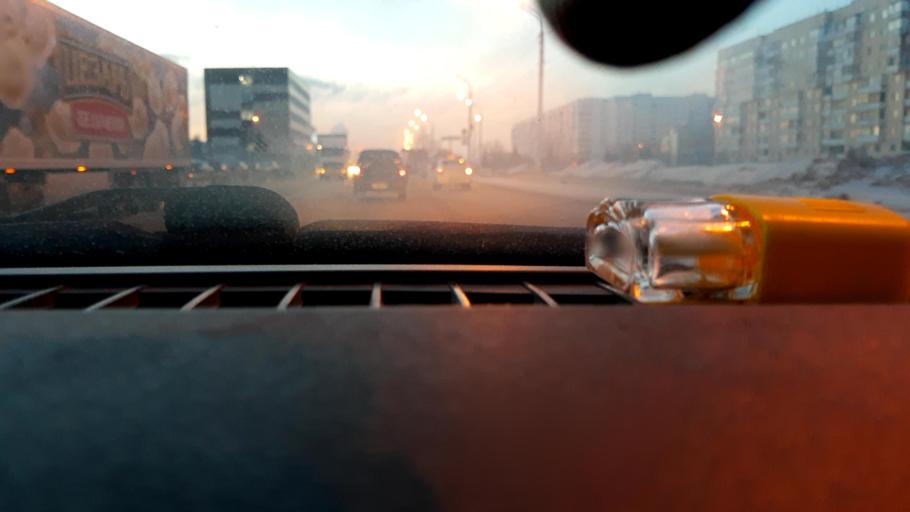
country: RU
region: Bashkortostan
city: Iglino
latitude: 54.7625
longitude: 56.2425
